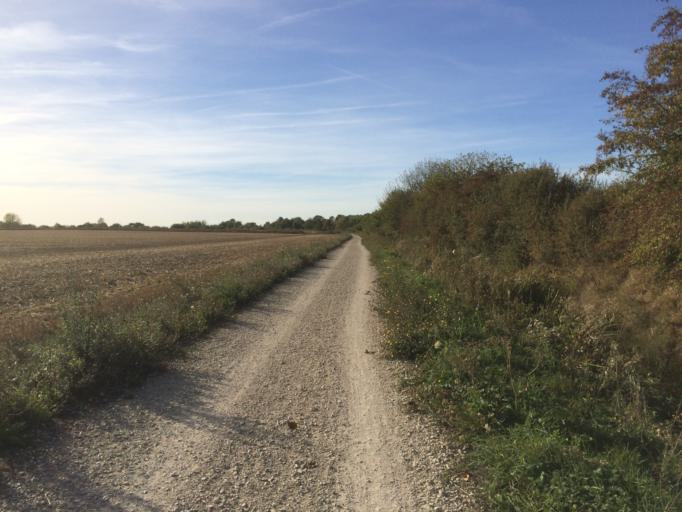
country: FR
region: Ile-de-France
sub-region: Departement de l'Essonne
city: Vauhallan
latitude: 48.7232
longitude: 2.2103
